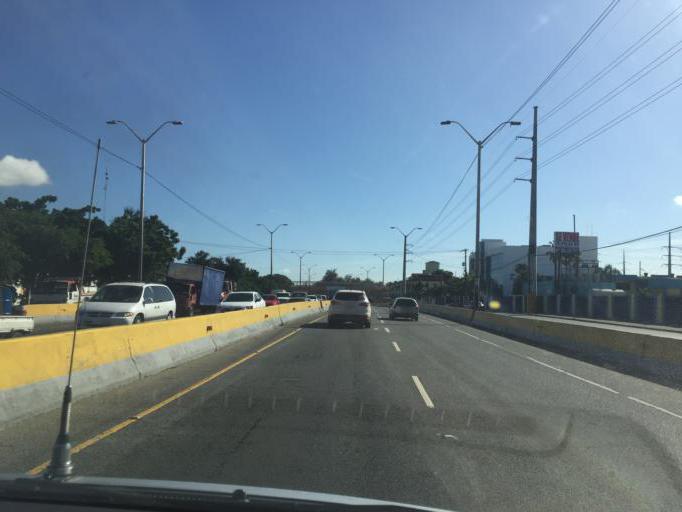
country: DO
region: Santo Domingo
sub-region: Santo Domingo
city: Santo Domingo Este
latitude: 18.4844
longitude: -69.8599
